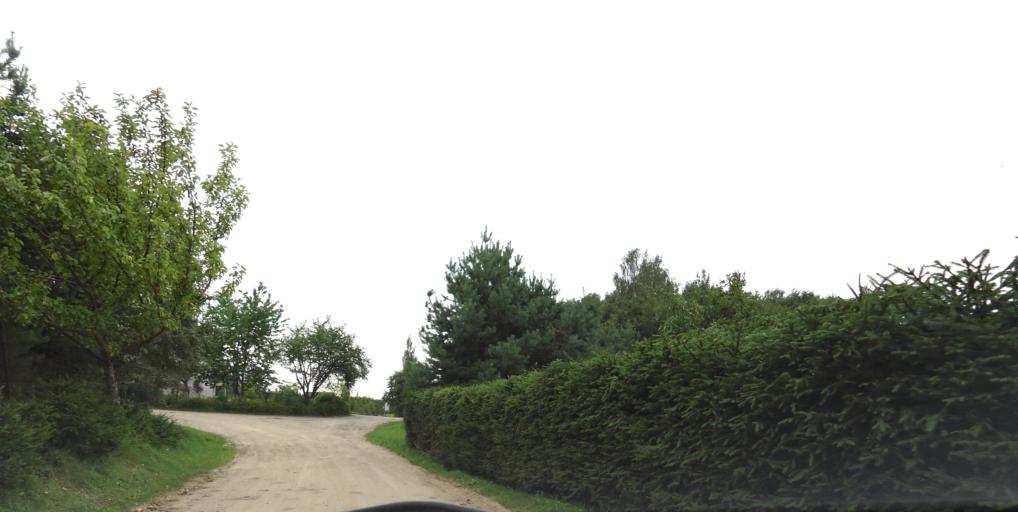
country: LT
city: Grigiskes
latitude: 54.7580
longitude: 25.0206
